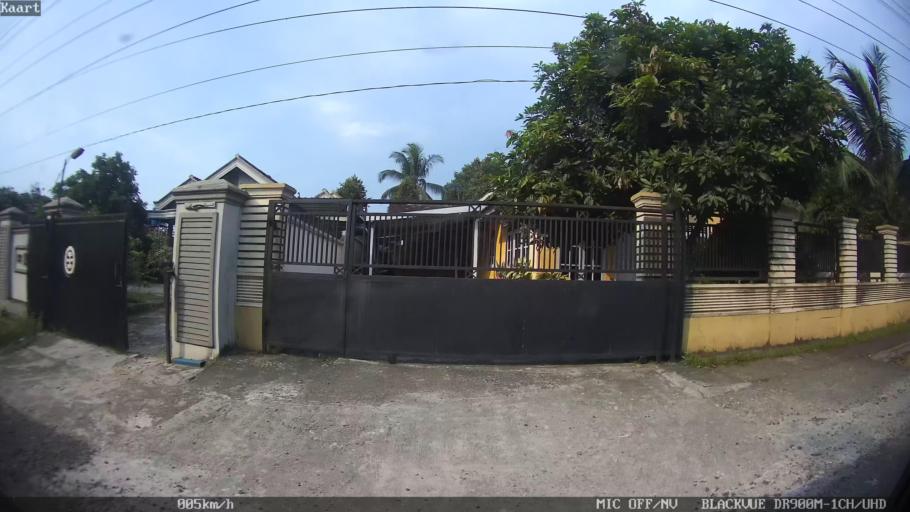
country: ID
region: Lampung
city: Natar
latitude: -5.3676
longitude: 105.1706
